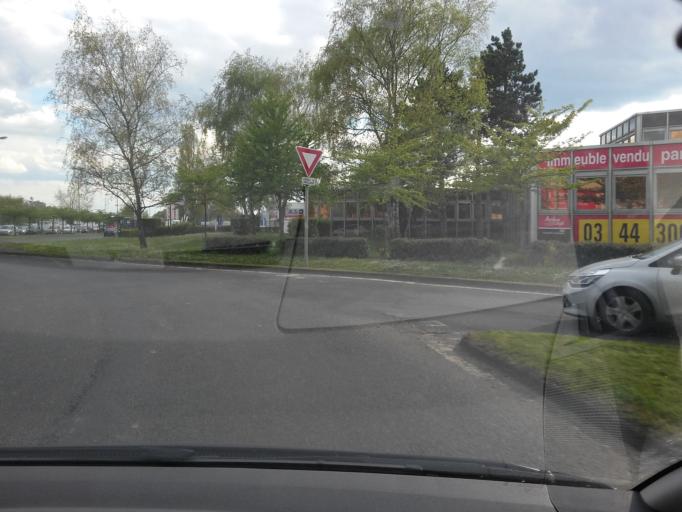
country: FR
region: Picardie
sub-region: Departement de l'Oise
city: Jaux
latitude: 49.3929
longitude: 2.7894
